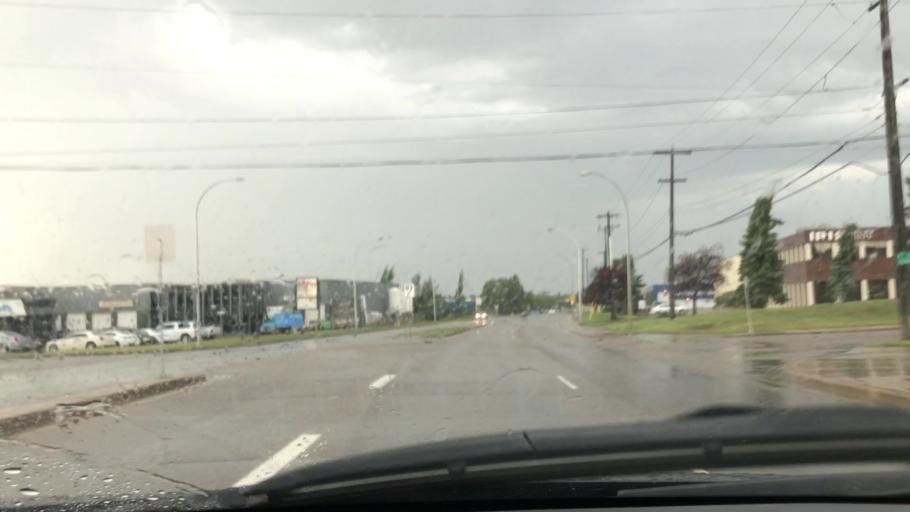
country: CA
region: Alberta
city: Edmonton
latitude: 53.4897
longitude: -113.4548
